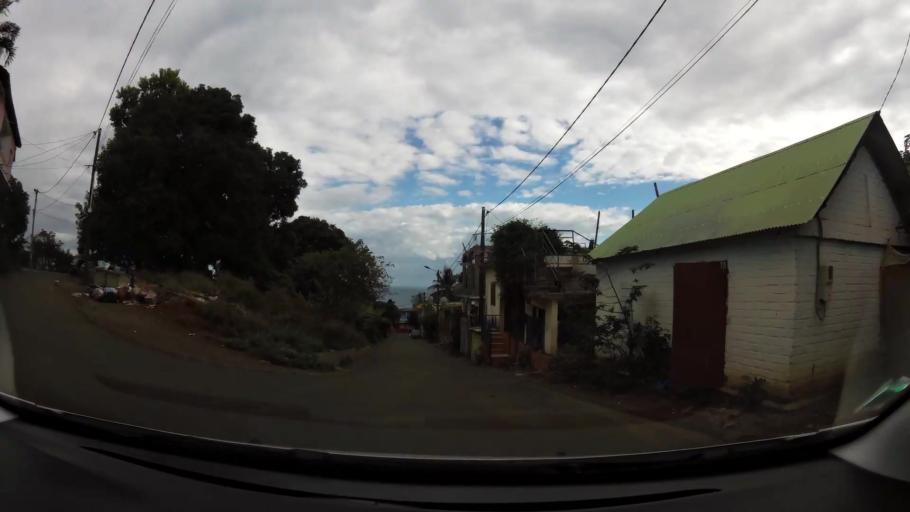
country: YT
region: Sada
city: Sada
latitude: -12.8476
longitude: 45.1054
